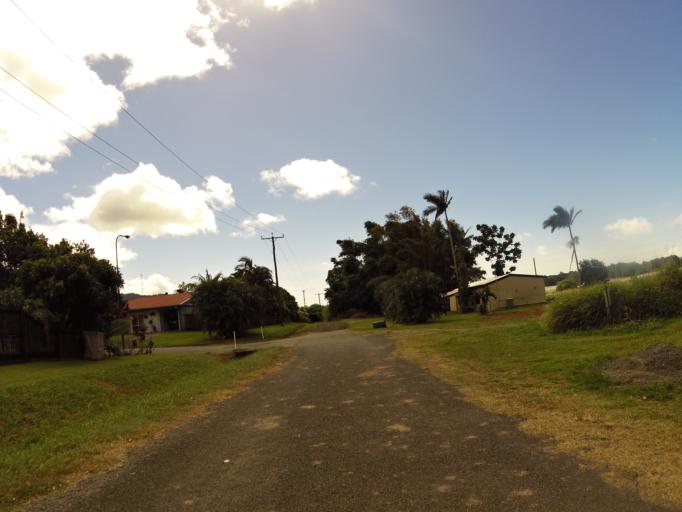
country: AU
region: Queensland
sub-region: Cairns
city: Redlynch
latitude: -16.8825
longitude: 145.6944
